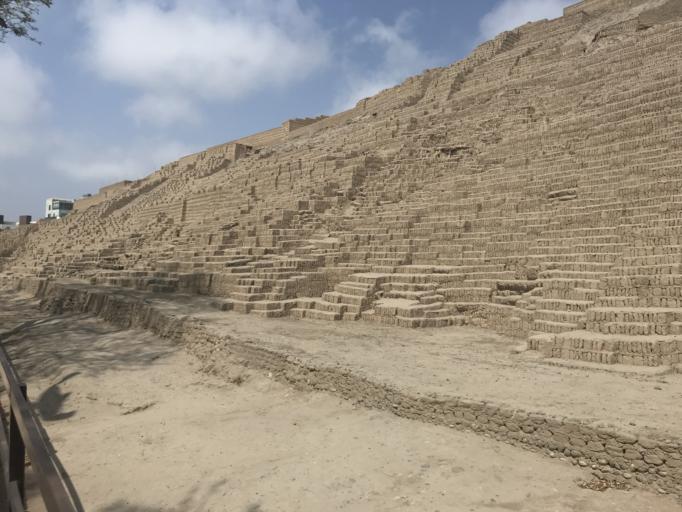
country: PE
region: Lima
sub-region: Lima
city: San Isidro
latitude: -12.1113
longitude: -77.0344
